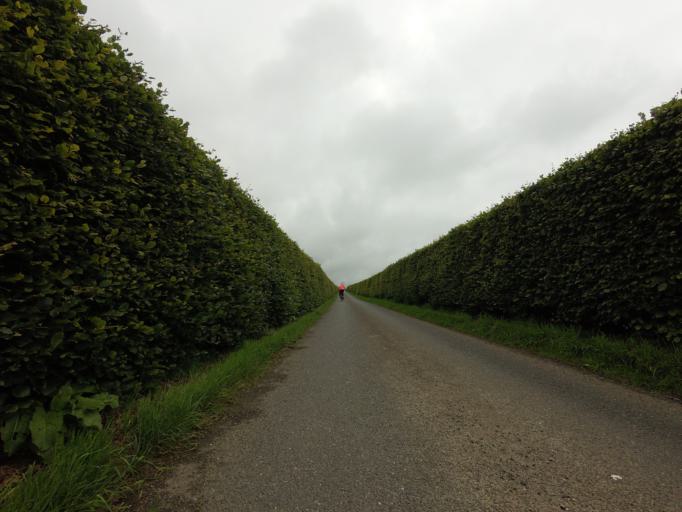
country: GB
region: Scotland
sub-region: Aberdeenshire
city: Turriff
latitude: 57.5436
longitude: -2.2985
